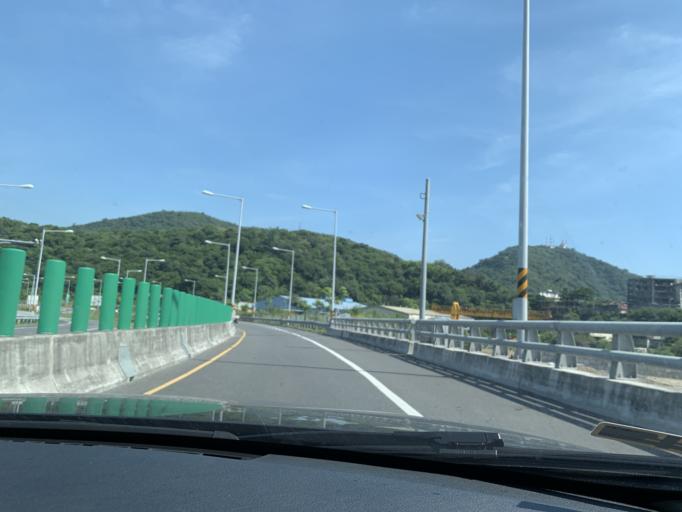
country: TW
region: Taiwan
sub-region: Yilan
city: Yilan
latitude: 24.5895
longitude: 121.8495
